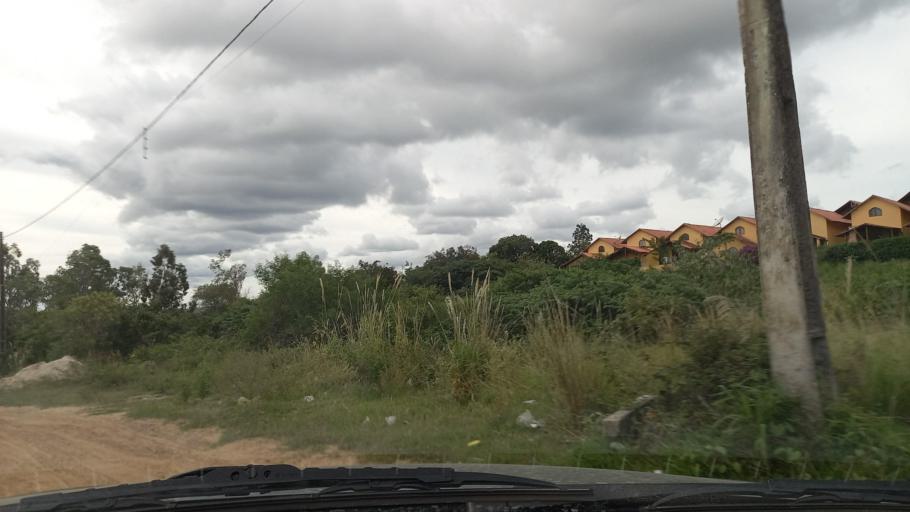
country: BR
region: Pernambuco
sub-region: Gravata
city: Gravata
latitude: -8.2038
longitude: -35.5447
